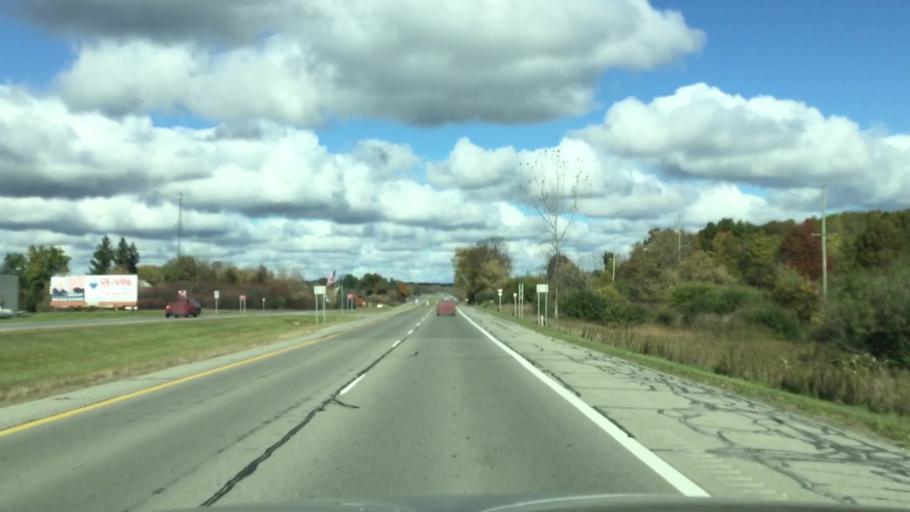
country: US
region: Michigan
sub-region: Oakland County
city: Oxford
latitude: 42.8526
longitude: -83.2829
